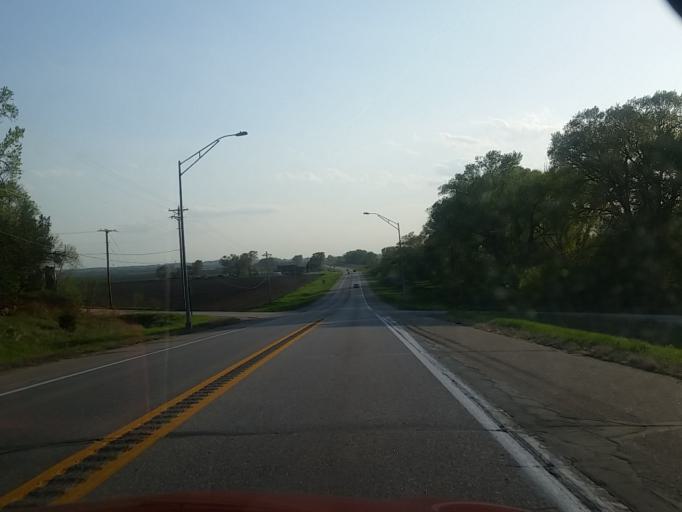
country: US
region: Nebraska
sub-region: Sarpy County
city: Gretna
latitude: 41.0874
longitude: -96.2814
